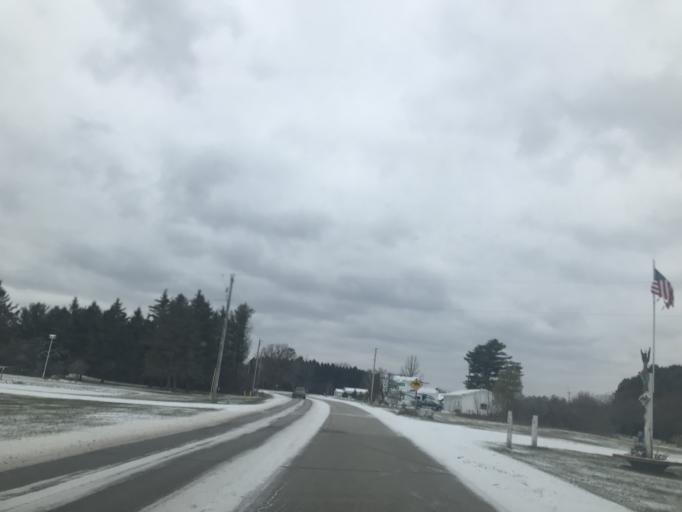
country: US
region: Wisconsin
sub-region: Marinette County
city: Peshtigo
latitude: 45.0588
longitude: -87.7094
